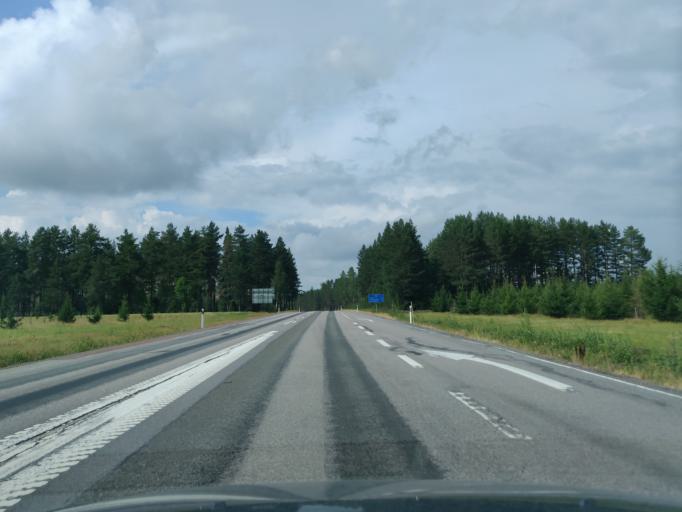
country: SE
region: Vaermland
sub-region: Hagfors Kommun
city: Hagfors
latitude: 60.0364
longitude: 13.5872
